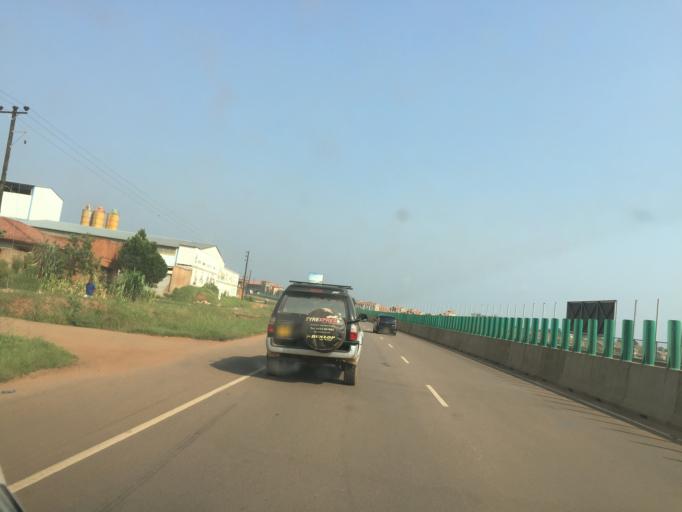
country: UG
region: Central Region
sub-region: Wakiso District
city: Kajansi
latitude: 0.2068
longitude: 32.5906
